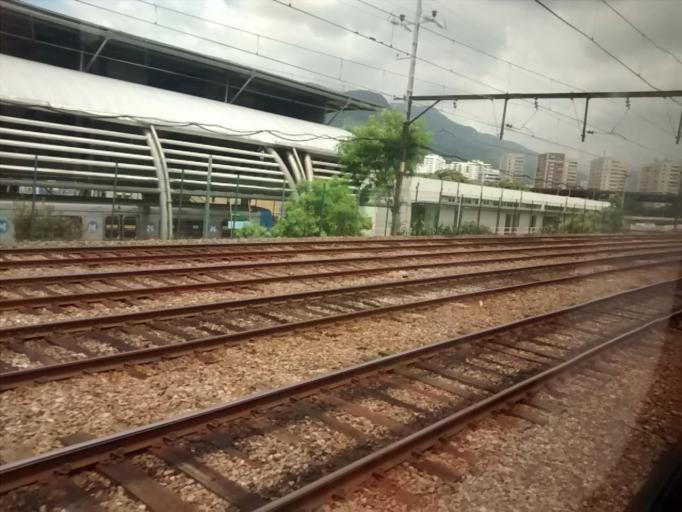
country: BR
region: Rio de Janeiro
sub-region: Rio De Janeiro
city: Rio de Janeiro
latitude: -22.9085
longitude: -43.2066
